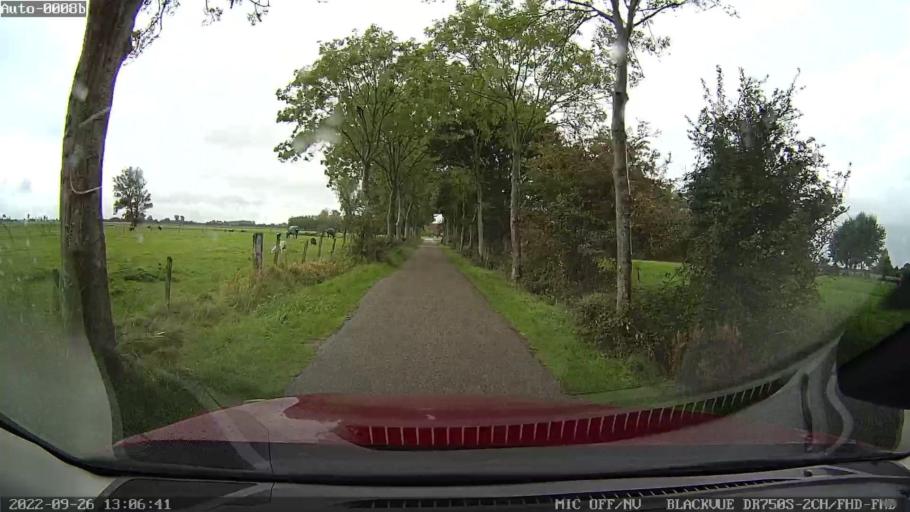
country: NL
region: Zeeland
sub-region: Gemeente Middelburg
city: Middelburg
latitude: 51.5492
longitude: 3.5883
